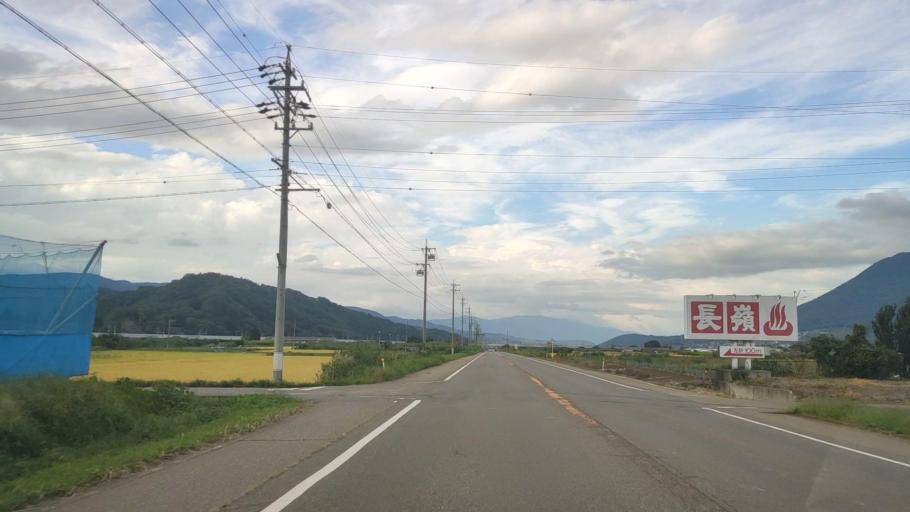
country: JP
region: Nagano
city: Nakano
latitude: 36.7724
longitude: 138.3505
